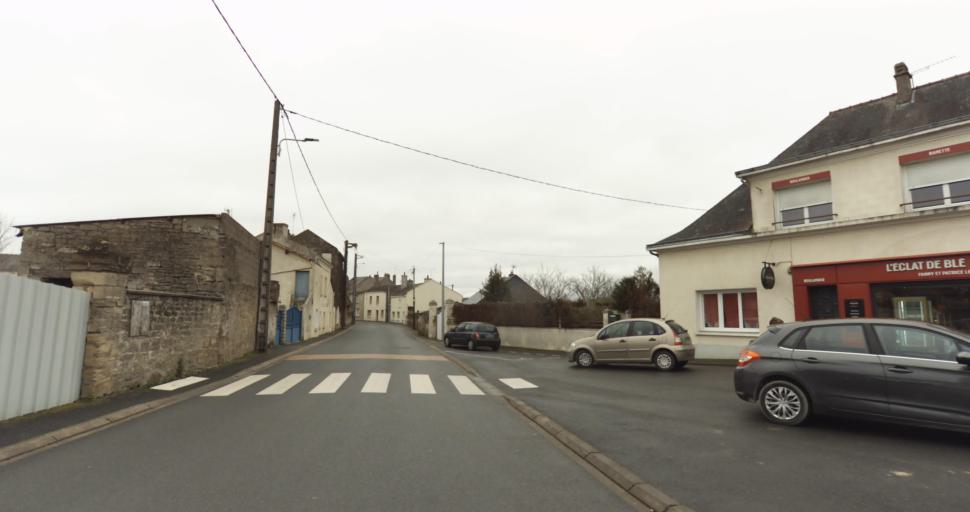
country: FR
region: Pays de la Loire
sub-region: Departement de Maine-et-Loire
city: Doue-la-Fontaine
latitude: 47.1885
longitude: -0.2668
